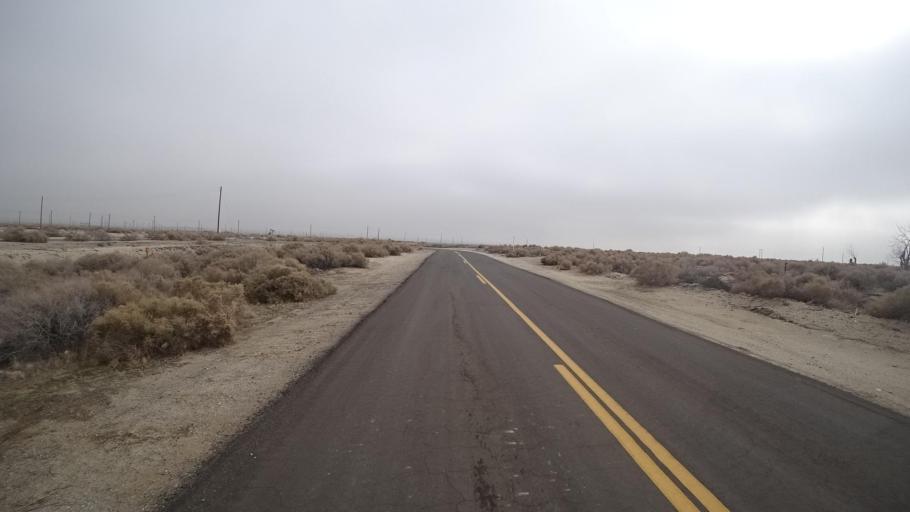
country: US
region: California
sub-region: Kern County
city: Maricopa
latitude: 35.0790
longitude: -119.3807
